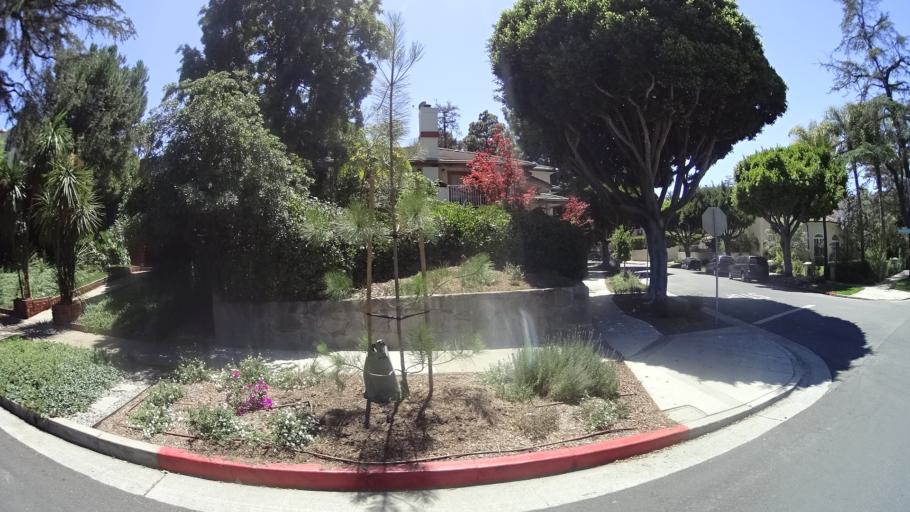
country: US
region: California
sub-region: Los Angeles County
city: Santa Monica
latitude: 34.0448
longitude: -118.4943
